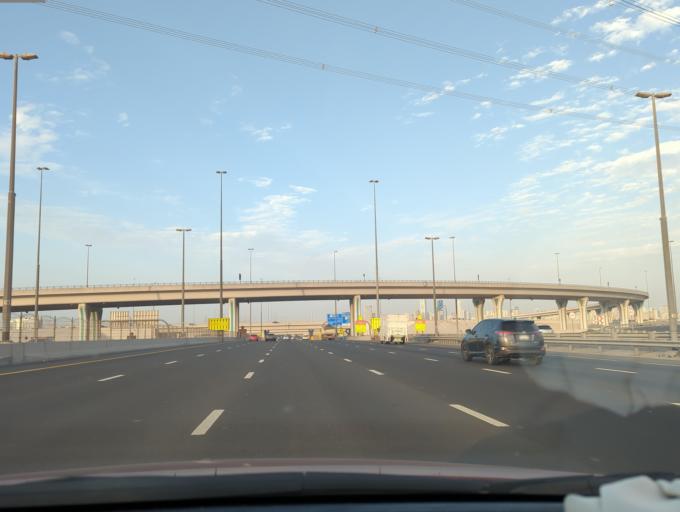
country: AE
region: Dubai
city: Dubai
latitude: 25.0141
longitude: 55.1581
